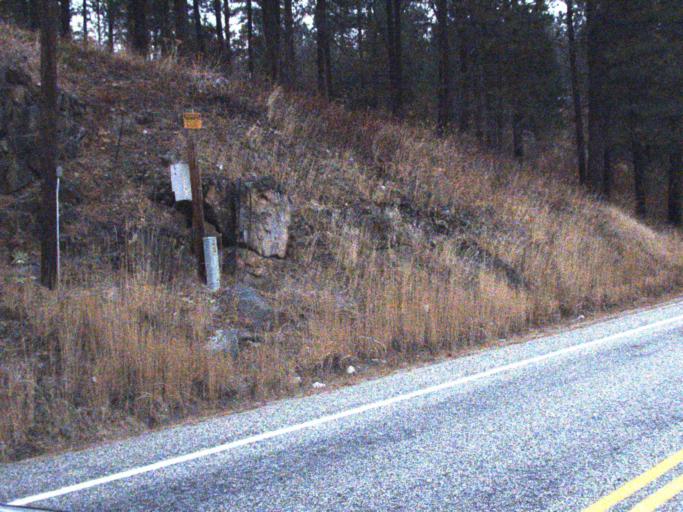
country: US
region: Washington
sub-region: Stevens County
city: Kettle Falls
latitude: 48.7491
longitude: -118.1350
